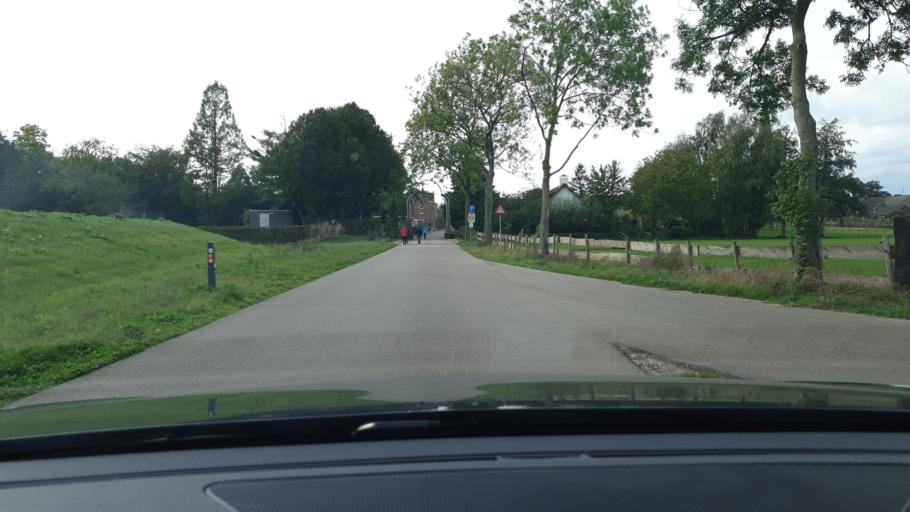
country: NL
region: Limburg
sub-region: Gemeente Venlo
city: Arcen
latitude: 51.4603
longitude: 6.1661
